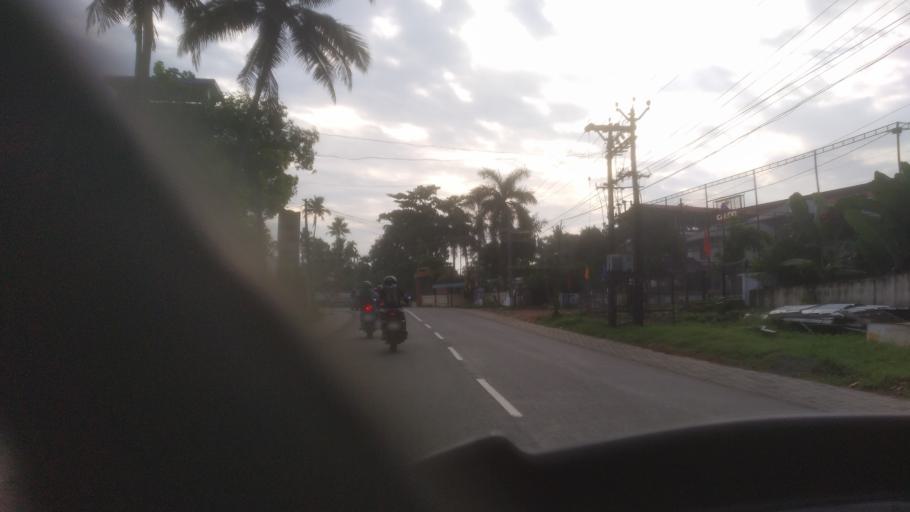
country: IN
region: Kerala
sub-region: Ernakulam
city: Kotamangalam
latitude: 10.0592
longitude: 76.6383
